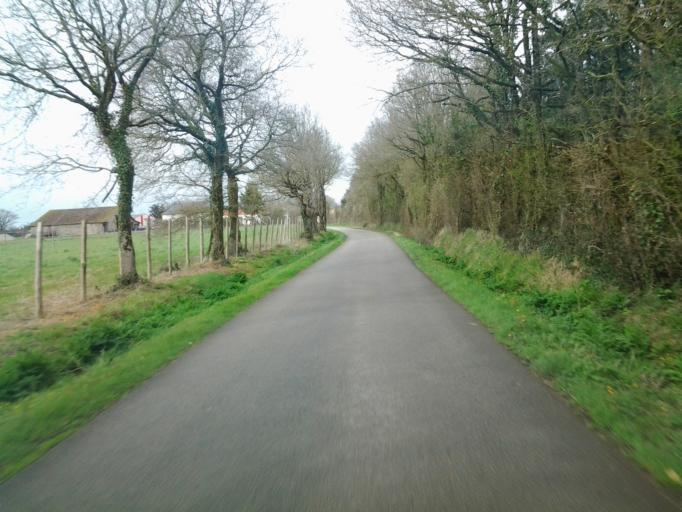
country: FR
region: Pays de la Loire
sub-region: Departement de la Vendee
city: Avrille
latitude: 46.4982
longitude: -1.4660
